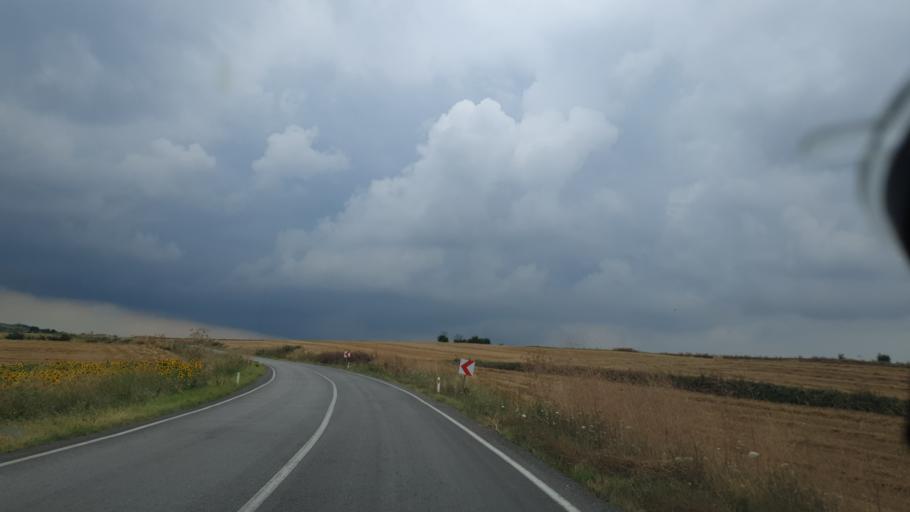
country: TR
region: Tekirdag
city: Hayrabolu
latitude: 41.2286
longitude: 27.0352
